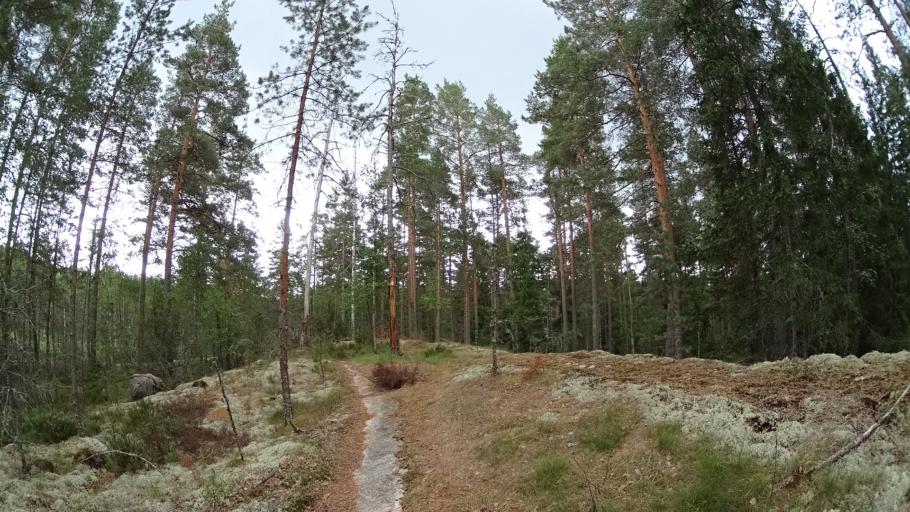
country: FI
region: Uusimaa
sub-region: Helsinki
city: Espoo
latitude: 60.3054
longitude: 24.5727
